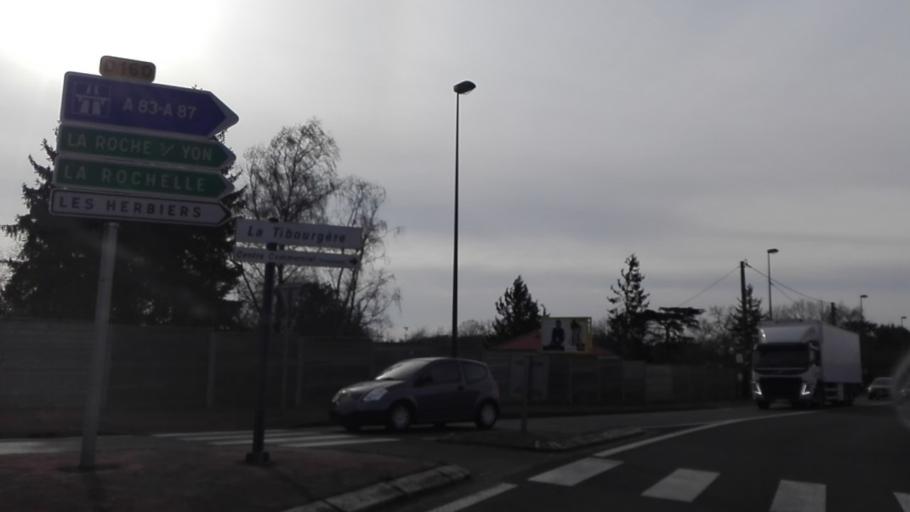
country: FR
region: Pays de la Loire
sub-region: Departement de la Vendee
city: Les Herbiers
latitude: 46.8821
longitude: -1.0107
